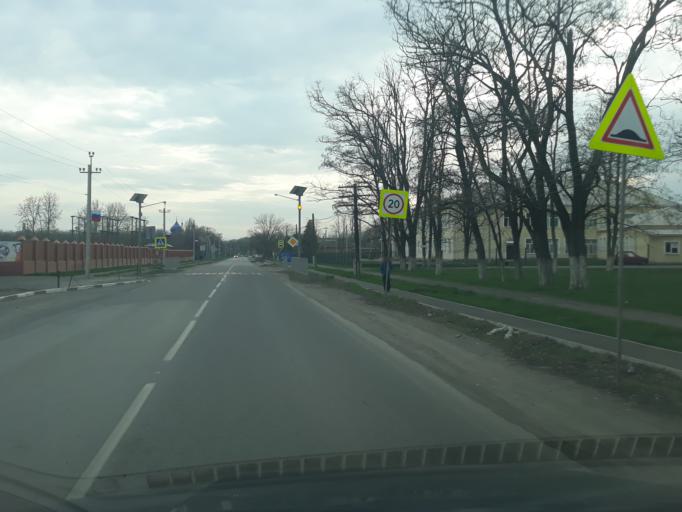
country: RU
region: Rostov
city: Novobessergenovka
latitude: 47.1684
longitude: 38.7411
